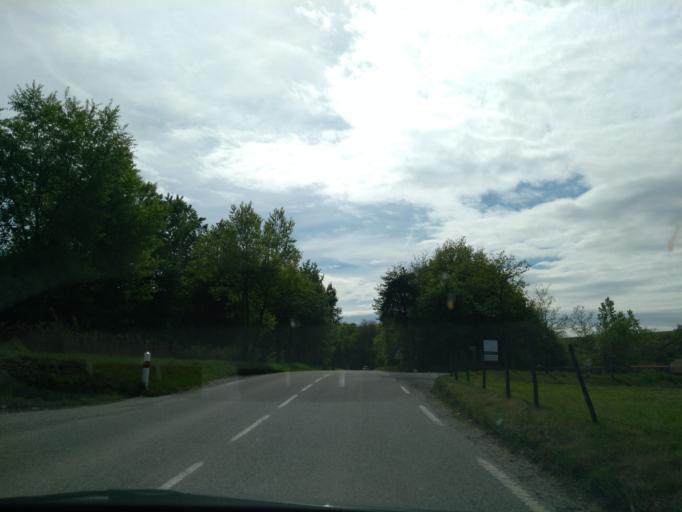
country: FR
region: Rhone-Alpes
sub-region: Departement de la Haute-Savoie
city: Chavanod
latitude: 45.8803
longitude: 6.0288
